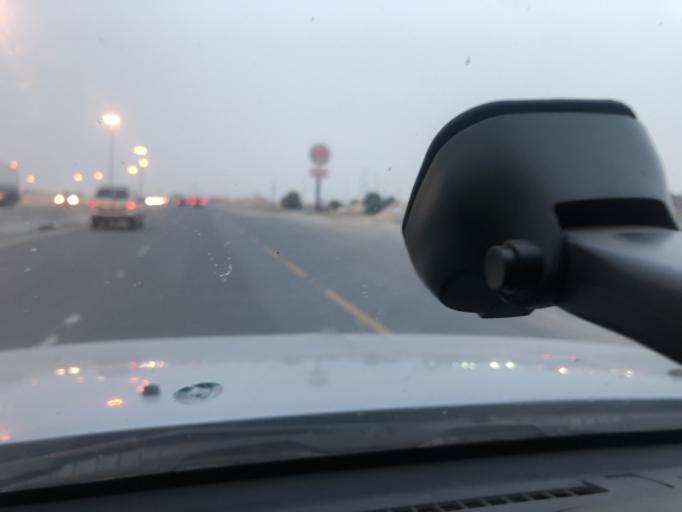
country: KW
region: Muhafazat al Jahra'
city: Al Jahra'
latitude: 29.4093
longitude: 47.6430
